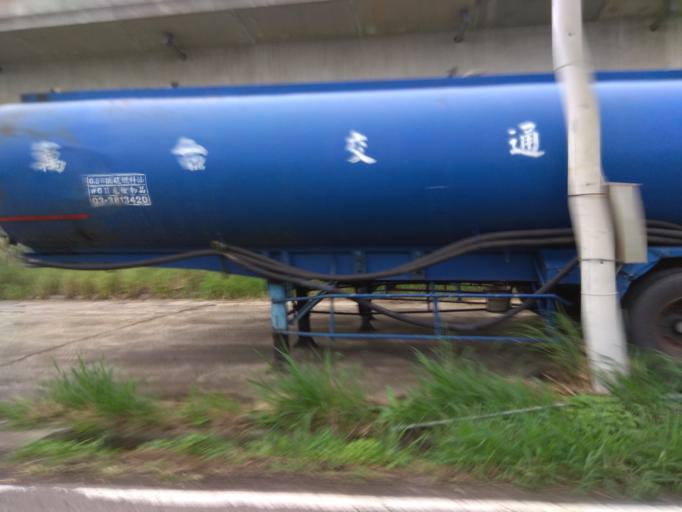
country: TW
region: Taiwan
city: Taoyuan City
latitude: 25.0461
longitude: 121.2146
